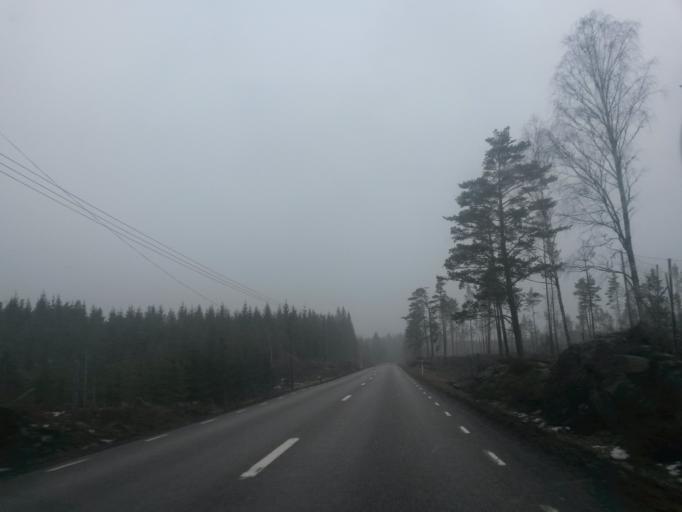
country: SE
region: Vaestra Goetaland
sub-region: Alingsas Kommun
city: Sollebrunn
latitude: 58.1976
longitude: 12.4310
